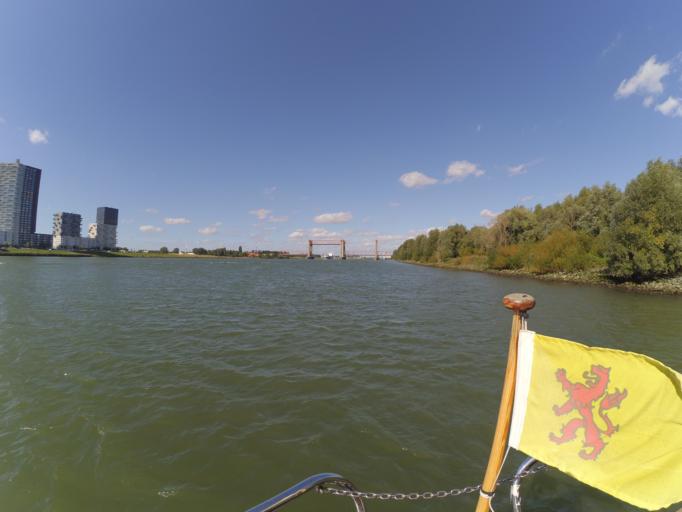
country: NL
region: South Holland
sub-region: Gemeente Spijkenisse
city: Spijkenisse
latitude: 51.8536
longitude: 4.3489
